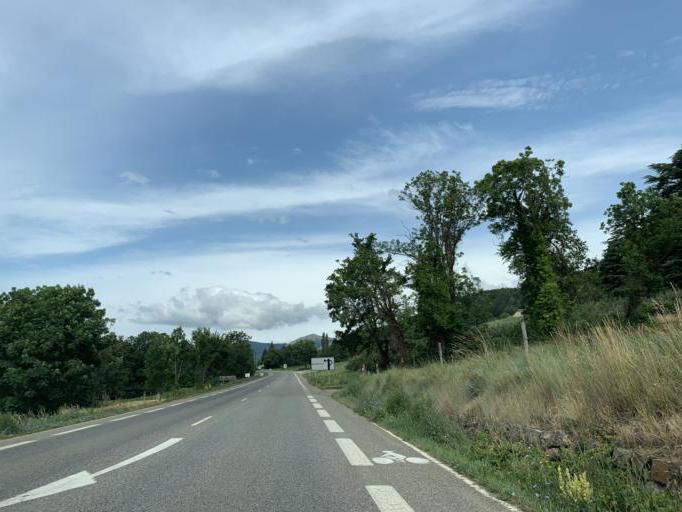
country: FR
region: Provence-Alpes-Cote d'Azur
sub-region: Departement des Hautes-Alpes
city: La Roche-des-Arnauds
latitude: 44.5432
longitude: 6.0093
